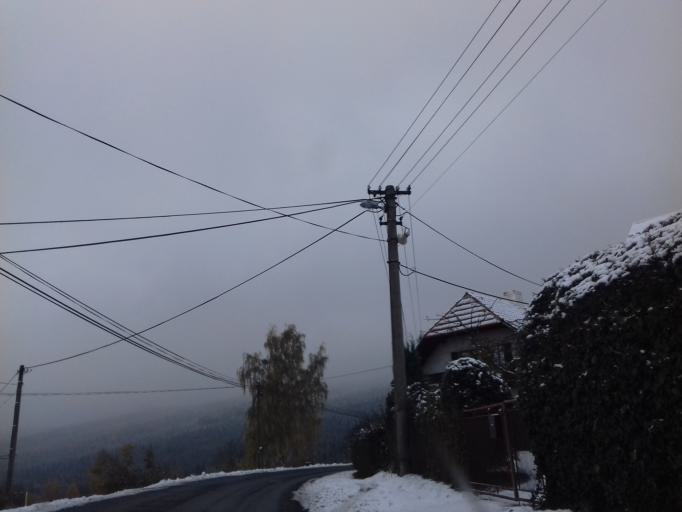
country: CZ
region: Plzensky
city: Postrekov
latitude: 49.4452
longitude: 12.7871
